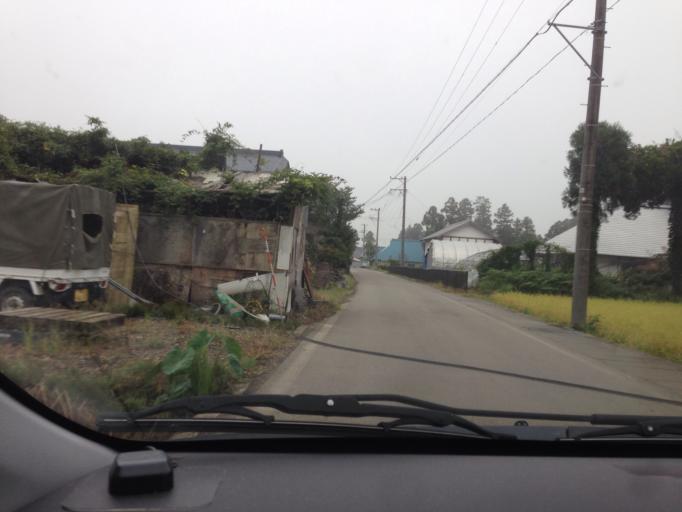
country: JP
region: Fukushima
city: Kitakata
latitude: 37.5909
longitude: 139.8739
